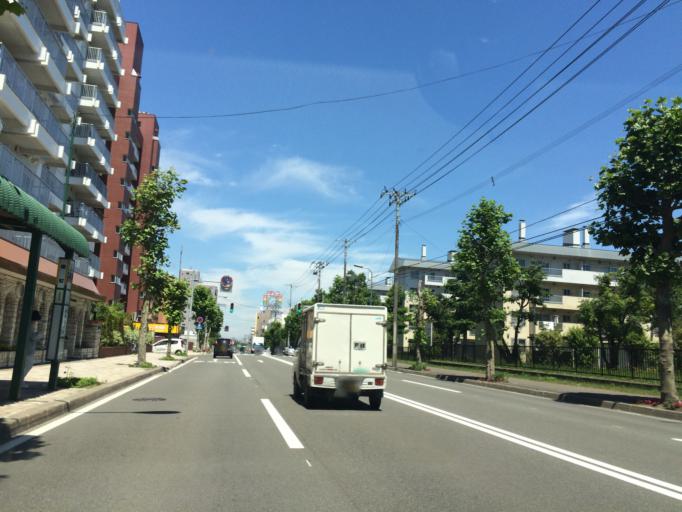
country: JP
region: Hokkaido
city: Sapporo
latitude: 43.0016
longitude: 141.3483
